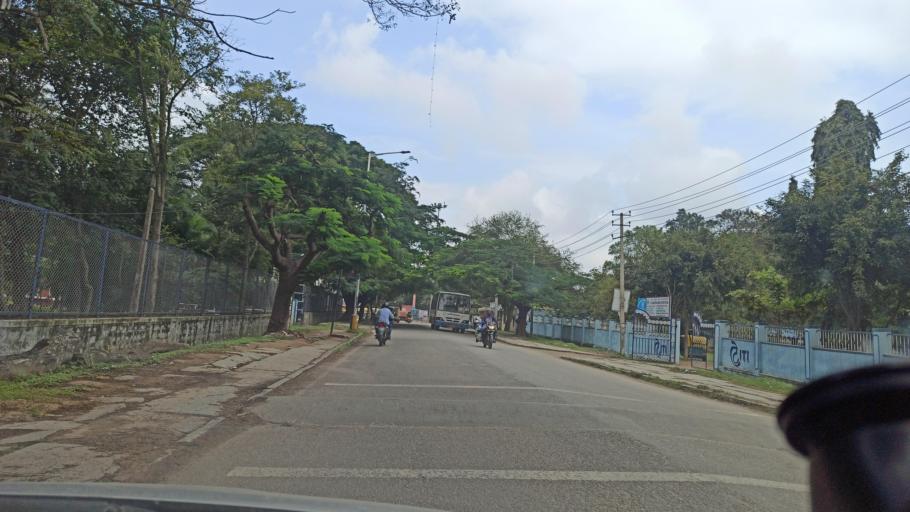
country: IN
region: Karnataka
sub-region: Bangalore Urban
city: Bangalore
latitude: 13.0067
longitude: 77.6840
